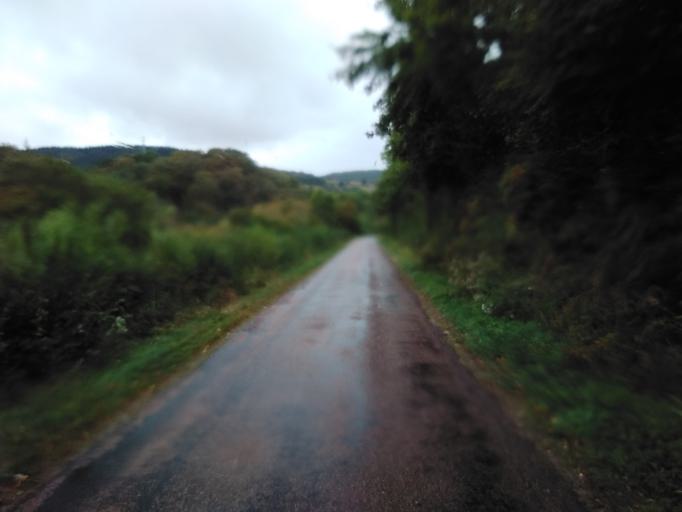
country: FR
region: Bourgogne
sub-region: Departement de la Nievre
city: Lormes
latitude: 47.3379
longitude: 3.9224
